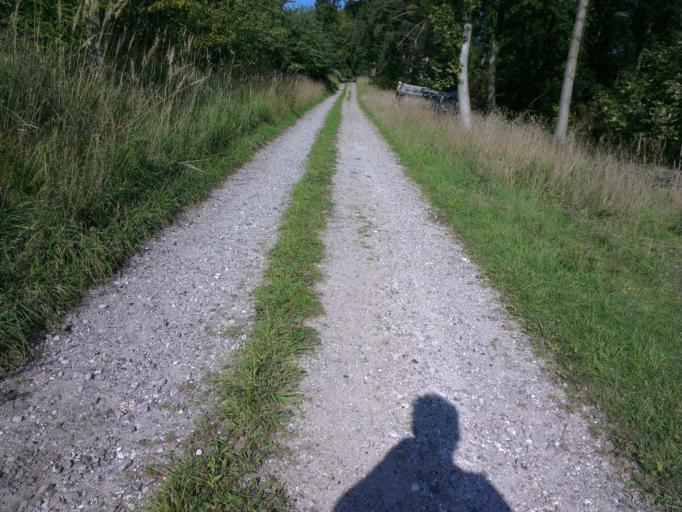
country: DK
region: Capital Region
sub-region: Frederikssund Kommune
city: Frederikssund
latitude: 55.8492
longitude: 12.0203
